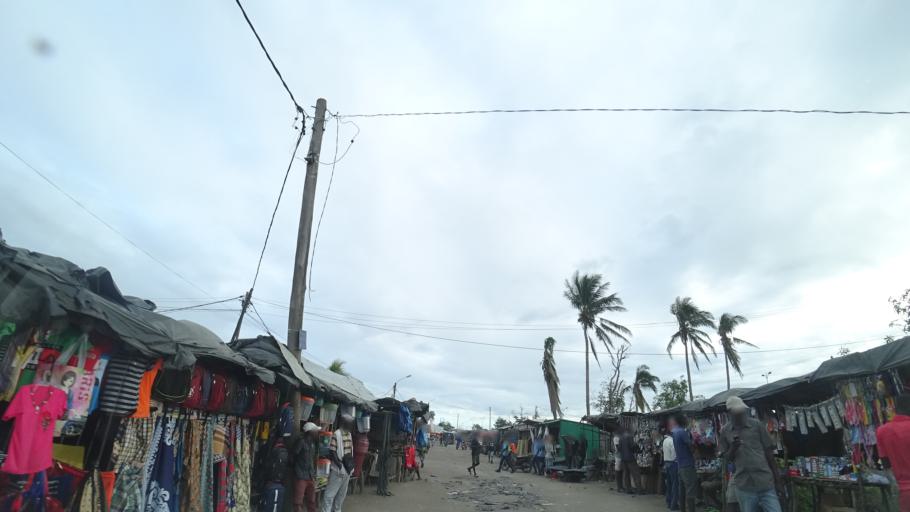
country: MZ
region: Sofala
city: Beira
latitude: -19.7757
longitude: 34.8837
